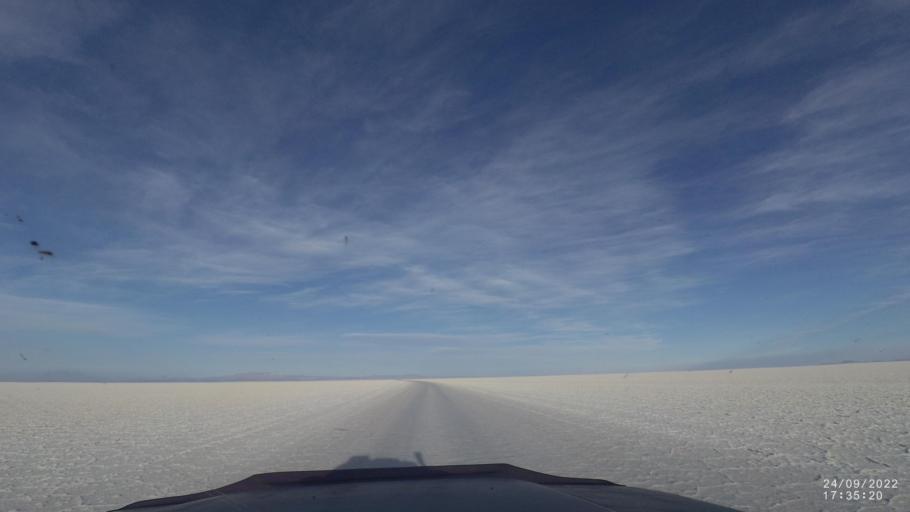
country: BO
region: Potosi
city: Colchani
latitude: -20.3232
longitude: -67.2601
